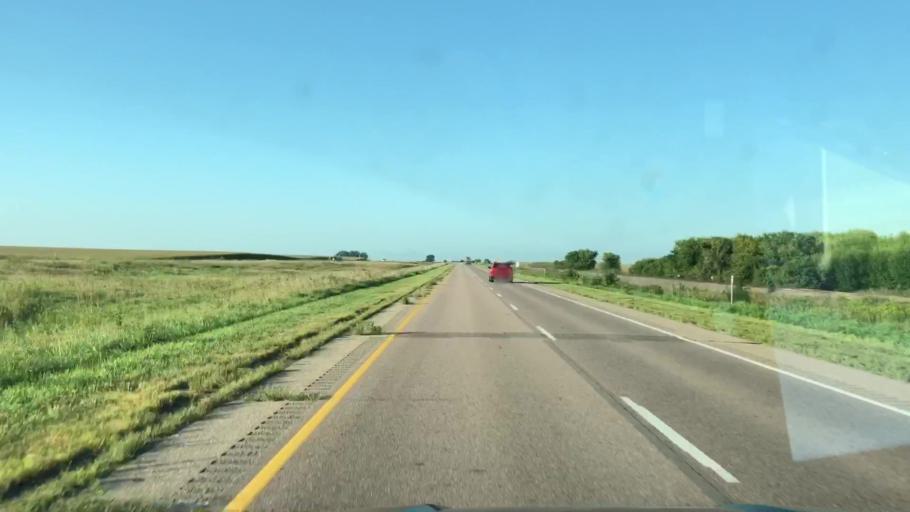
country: US
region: Iowa
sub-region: O'Brien County
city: Sheldon
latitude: 43.1170
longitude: -95.8930
